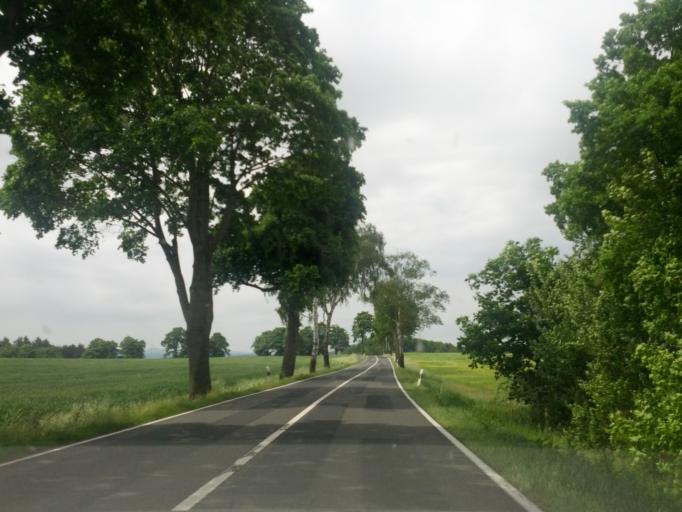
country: DE
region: Thuringia
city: Marksuhl
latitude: 50.9252
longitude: 10.2227
